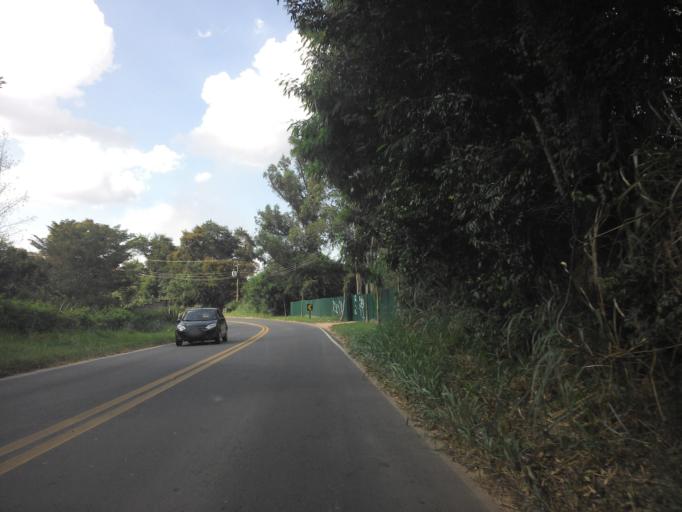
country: BR
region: Sao Paulo
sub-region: Vinhedo
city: Vinhedo
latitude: -23.0081
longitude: -47.0023
